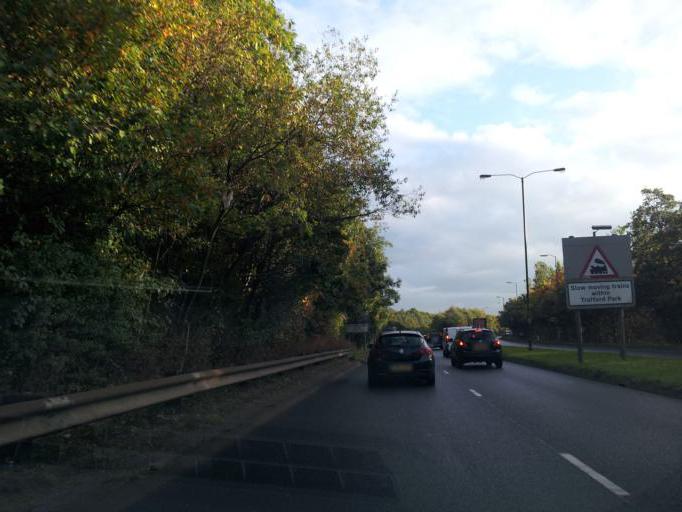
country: GB
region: England
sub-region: City and Borough of Salford
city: Eccles
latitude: 53.4659
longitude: -2.3309
